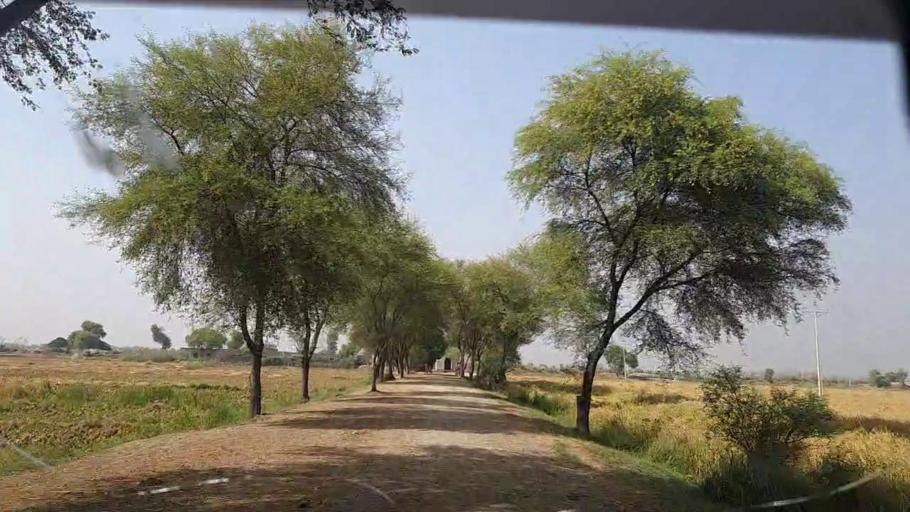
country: PK
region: Sindh
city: Shikarpur
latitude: 28.1156
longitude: 68.6572
